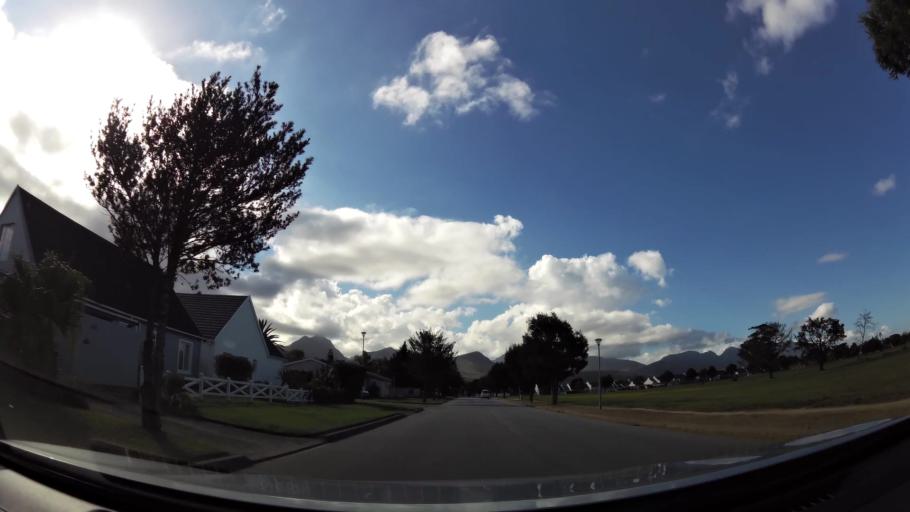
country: ZA
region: Western Cape
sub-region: Eden District Municipality
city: George
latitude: -33.9620
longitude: 22.4883
